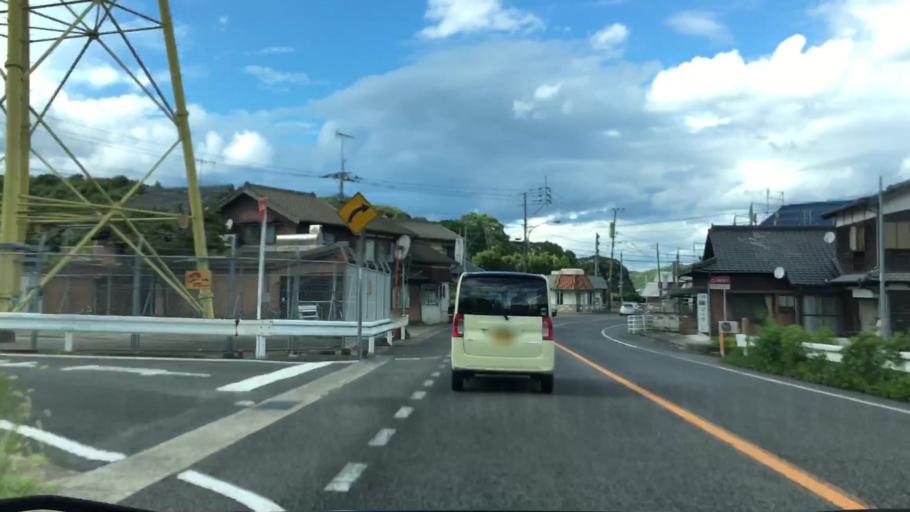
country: JP
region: Saga Prefecture
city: Imaricho-ko
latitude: 33.1783
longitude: 129.8519
